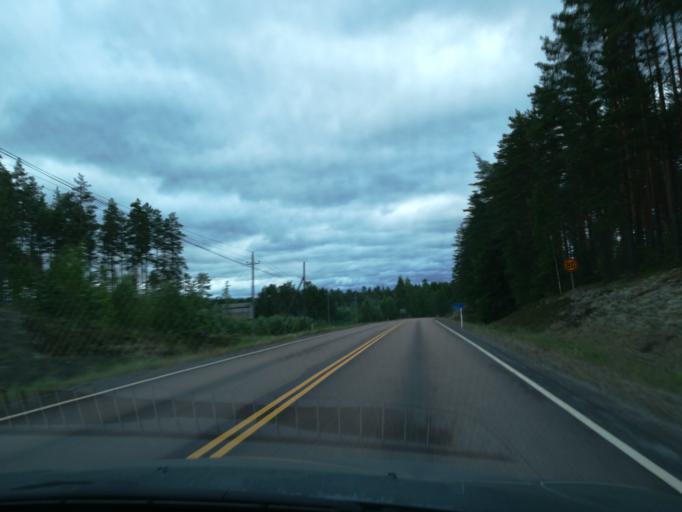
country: FI
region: Southern Savonia
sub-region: Mikkeli
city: Ristiina
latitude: 61.3470
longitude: 27.3752
